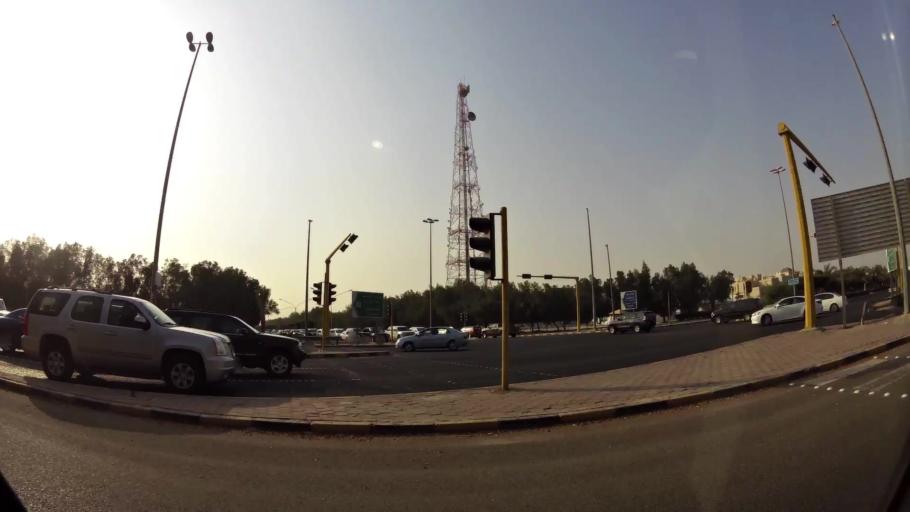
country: KW
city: Bayan
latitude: 29.2873
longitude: 48.0586
